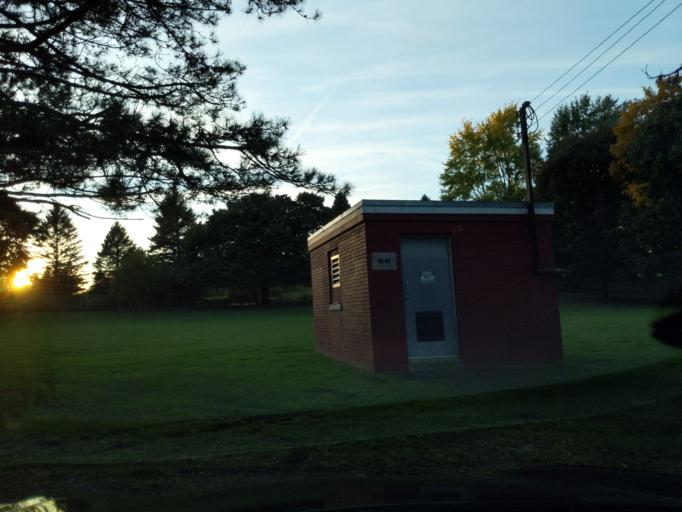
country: US
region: Michigan
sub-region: Ingham County
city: Edgemont Park
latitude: 42.7371
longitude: -84.5947
